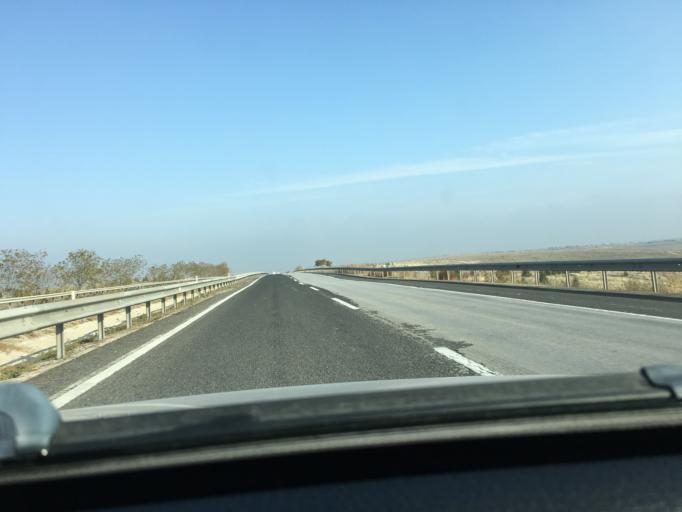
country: TR
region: Eskisehir
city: Gunyuzu
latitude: 39.5752
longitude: 31.9016
